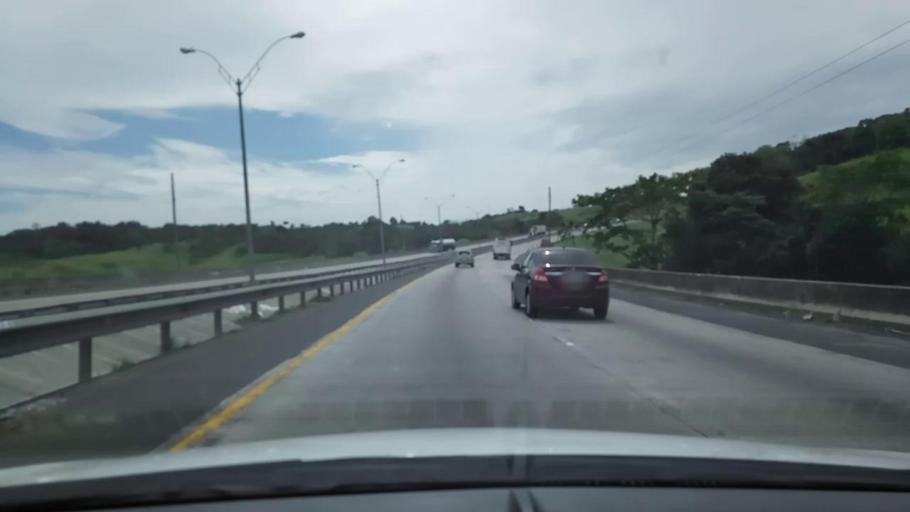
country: PA
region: Panama
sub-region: Distrito Arraijan
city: Arraijan
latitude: 8.9719
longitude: -79.6435
